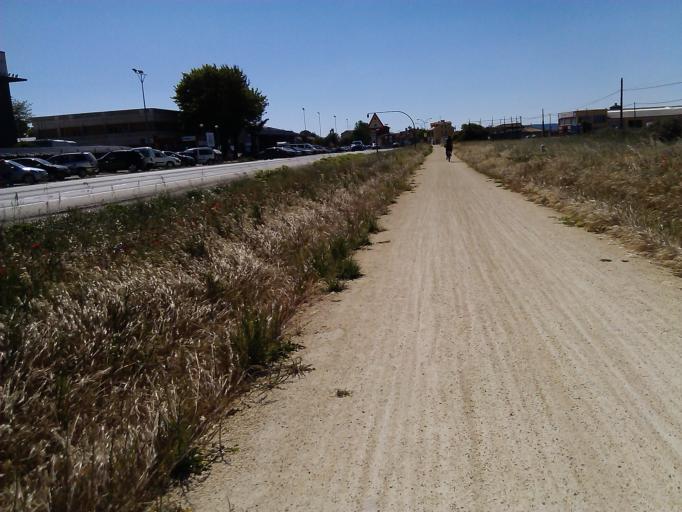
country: ES
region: Castille and Leon
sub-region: Provincia de Burgos
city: Cardenajimeno
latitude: 42.3432
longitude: -3.6219
